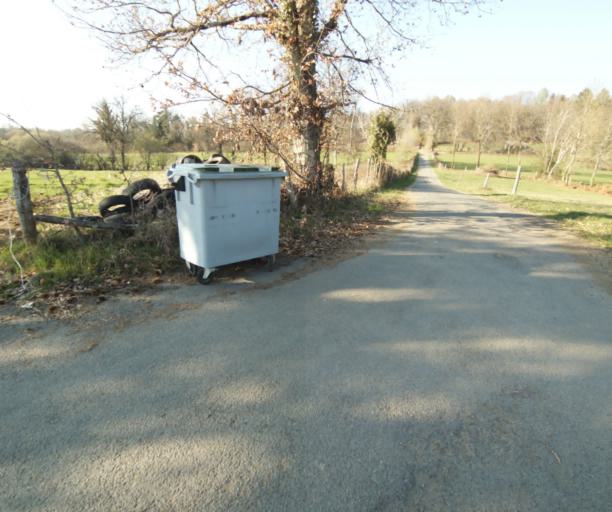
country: FR
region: Limousin
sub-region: Departement de la Correze
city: Saint-Clement
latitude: 45.3364
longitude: 1.6544
